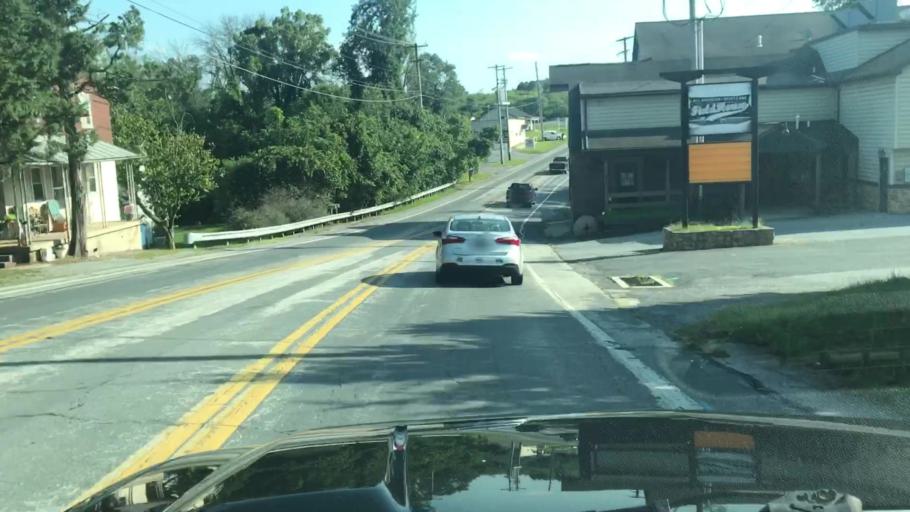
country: US
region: Pennsylvania
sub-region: York County
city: Valley Green
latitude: 40.1592
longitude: -76.8161
